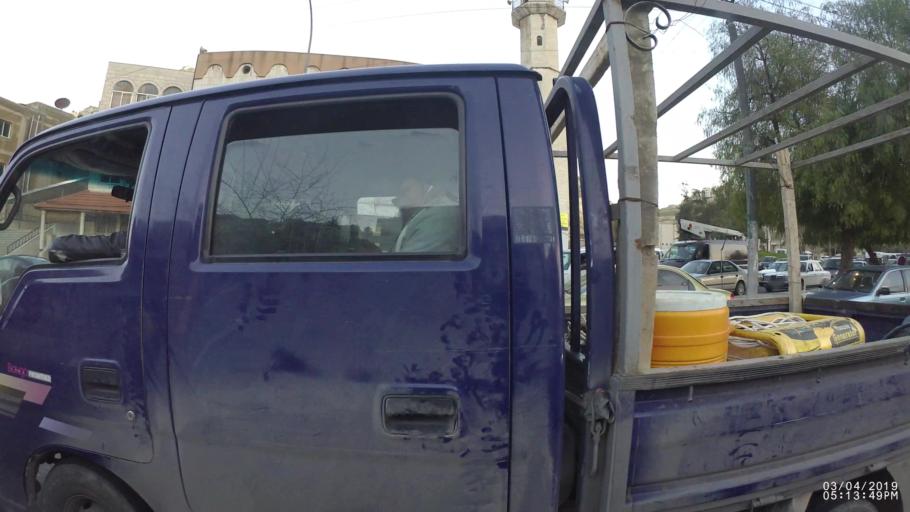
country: JO
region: Amman
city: Al Quwaysimah
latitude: 31.9318
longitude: 35.9217
